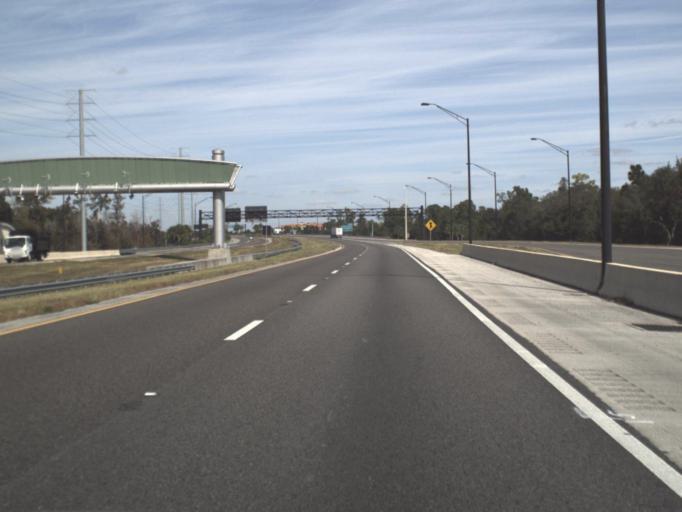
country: US
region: Florida
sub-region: Polk County
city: Citrus Ridge
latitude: 28.3603
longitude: -81.6113
